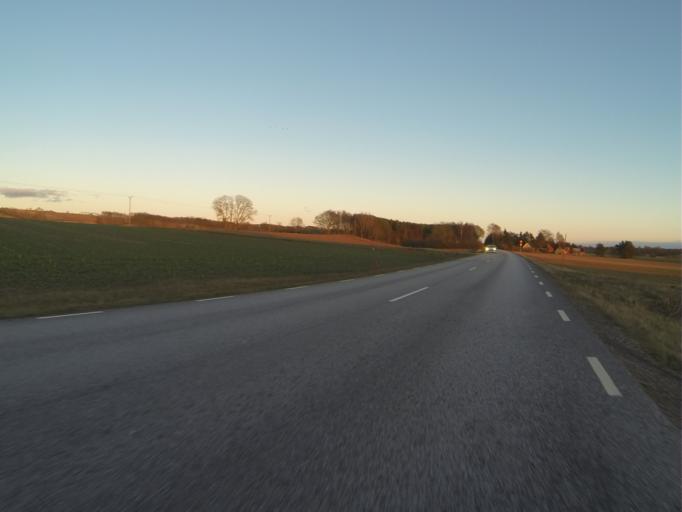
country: SE
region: Skane
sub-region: Hoors Kommun
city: Loberod
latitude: 55.7347
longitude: 13.4497
